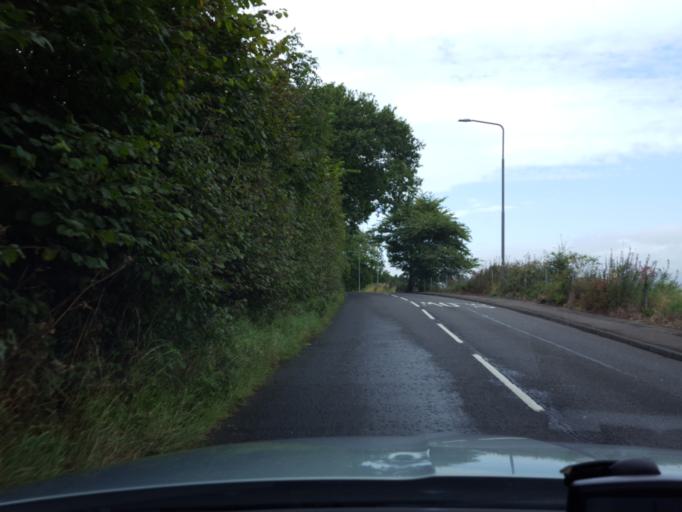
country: GB
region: Scotland
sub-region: Fife
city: Tayport
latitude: 56.4514
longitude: -2.8937
